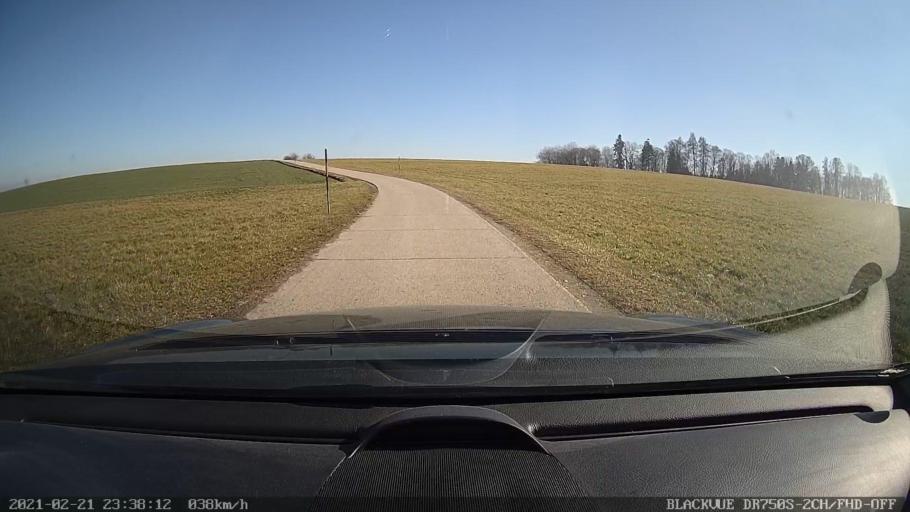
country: DE
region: Bavaria
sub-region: Upper Bavaria
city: Griesstatt
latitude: 47.9945
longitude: 12.2049
